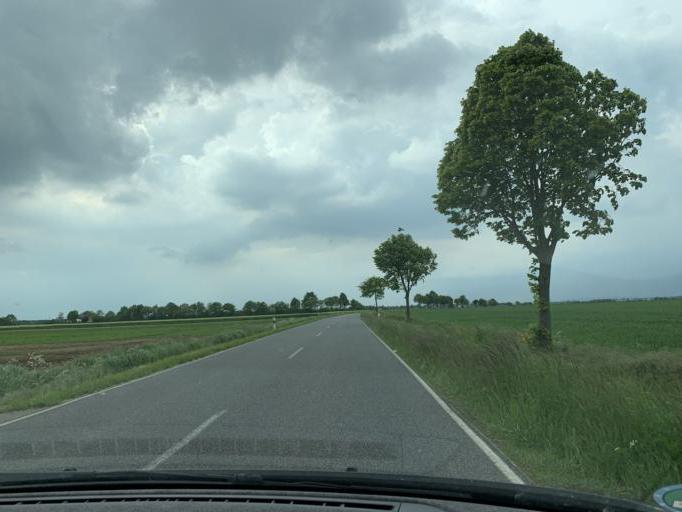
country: DE
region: North Rhine-Westphalia
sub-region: Regierungsbezirk Koln
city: Vettweiss
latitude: 50.7481
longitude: 6.5796
